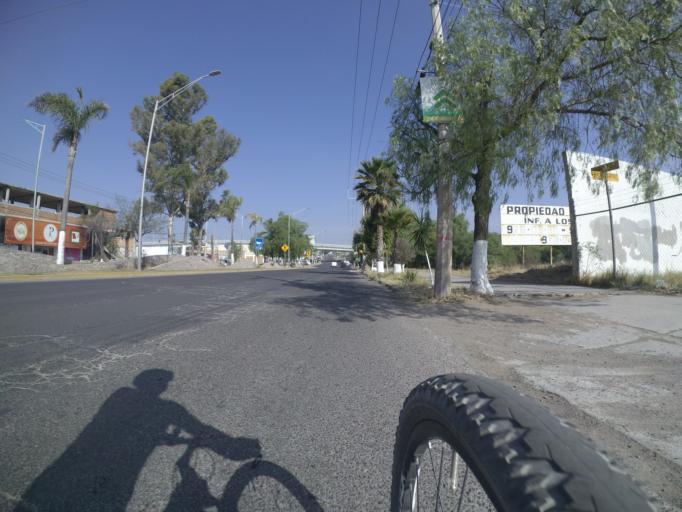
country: MX
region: Aguascalientes
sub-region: Jesus Maria
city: Corral de Barrancos
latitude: 21.9536
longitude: -102.3364
